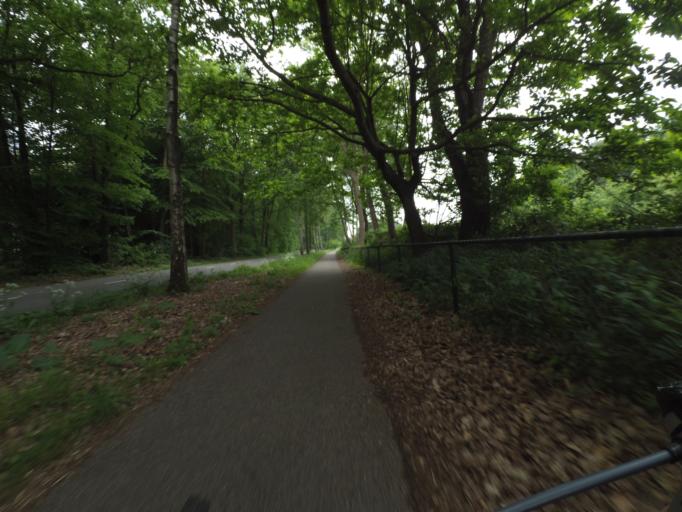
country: NL
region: Gelderland
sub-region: Gemeente Renkum
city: Wolfheze
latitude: 52.0064
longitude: 5.7871
